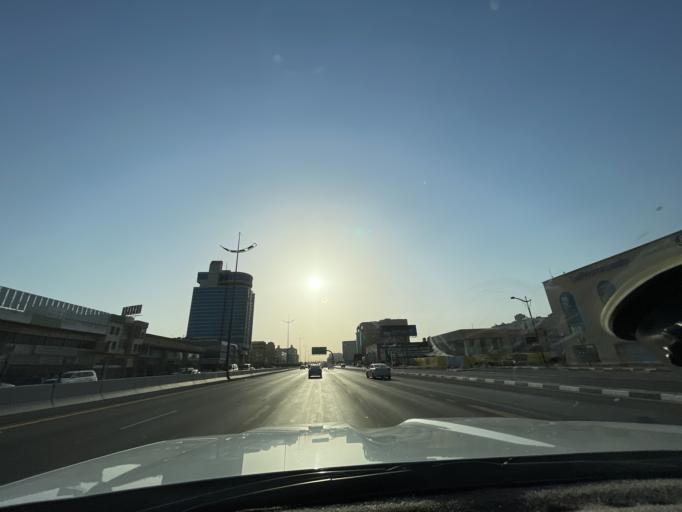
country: SA
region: Eastern Province
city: Khobar
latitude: 26.2846
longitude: 50.1954
